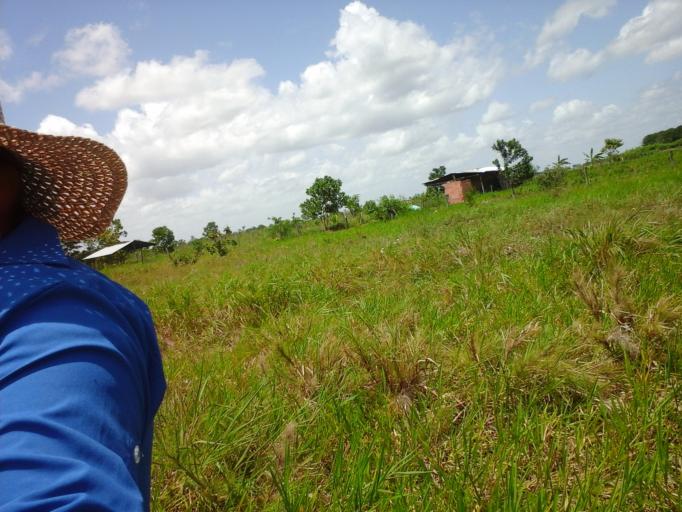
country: CO
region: Cundinamarca
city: Tibacuy
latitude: 4.2260
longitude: -72.4645
